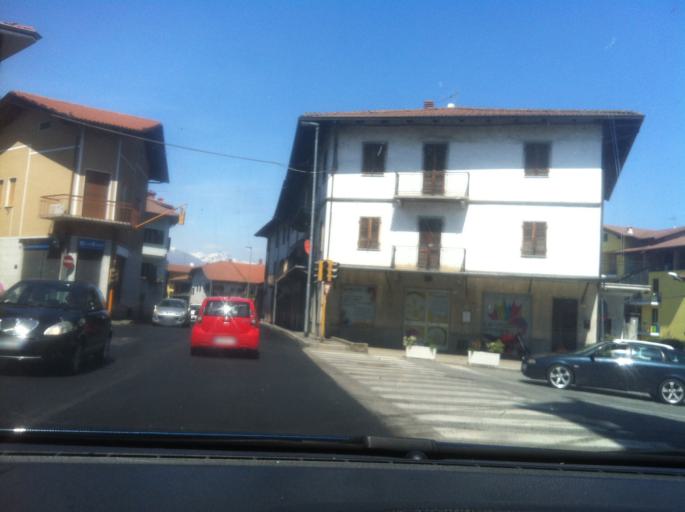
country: IT
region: Piedmont
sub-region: Provincia di Torino
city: Strambino
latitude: 45.3834
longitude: 7.8853
